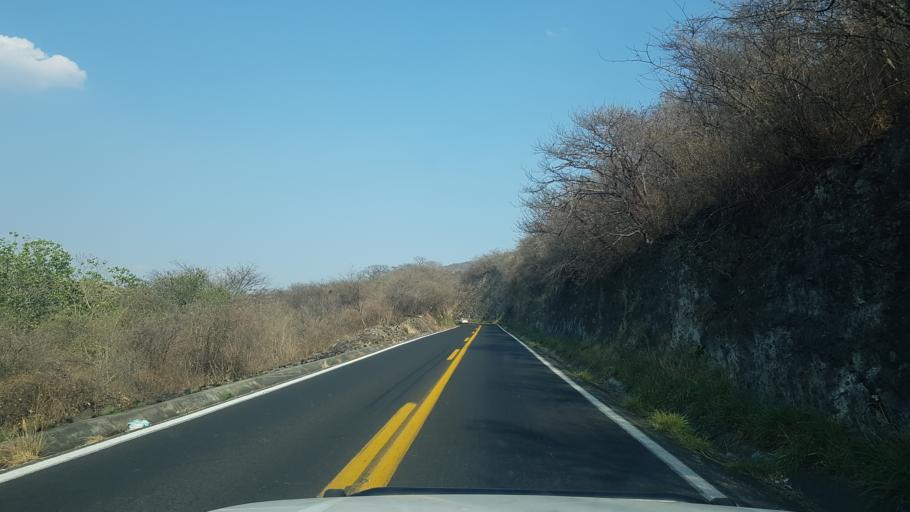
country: MX
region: Puebla
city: Calmeca
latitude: 18.6507
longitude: -98.6672
